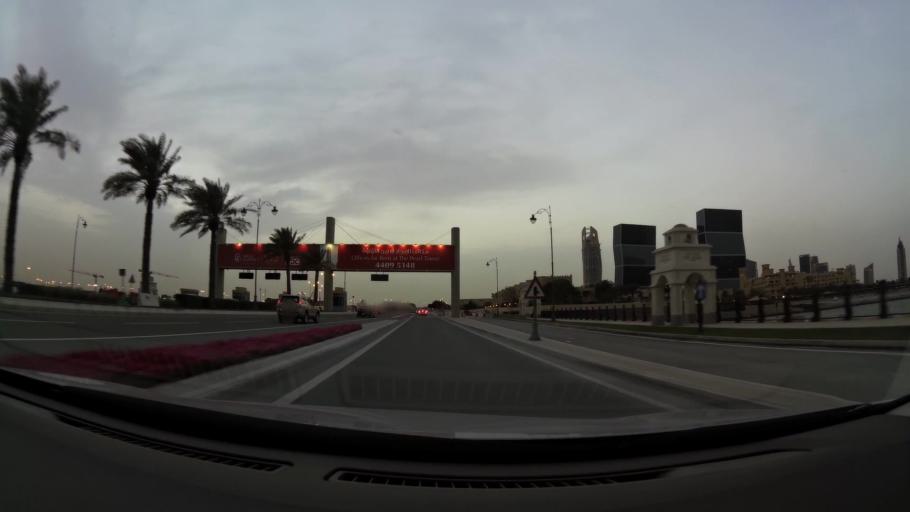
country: QA
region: Baladiyat ad Dawhah
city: Doha
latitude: 25.3730
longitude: 51.5300
